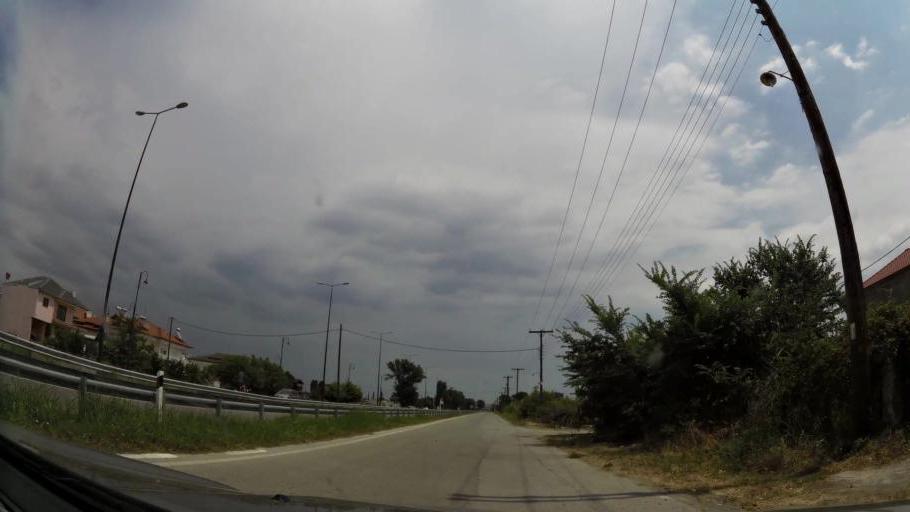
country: GR
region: Central Macedonia
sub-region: Nomos Pierias
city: Kallithea
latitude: 40.2693
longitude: 22.5811
